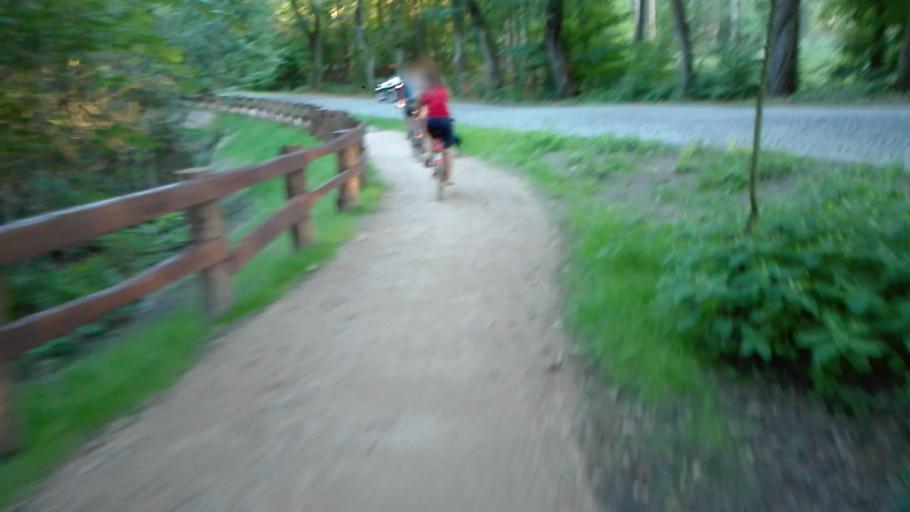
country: PL
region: West Pomeranian Voivodeship
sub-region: Powiat policki
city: Dobra
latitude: 53.4686
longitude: 14.3624
